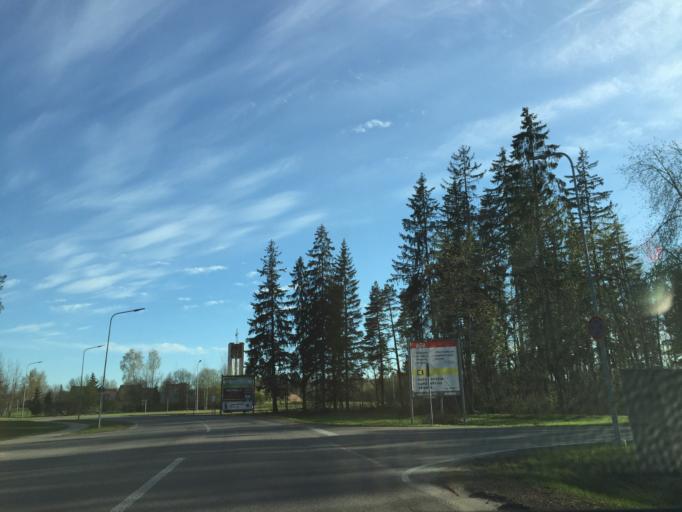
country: LV
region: Valkas Rajons
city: Valka
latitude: 57.7828
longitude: 25.9917
